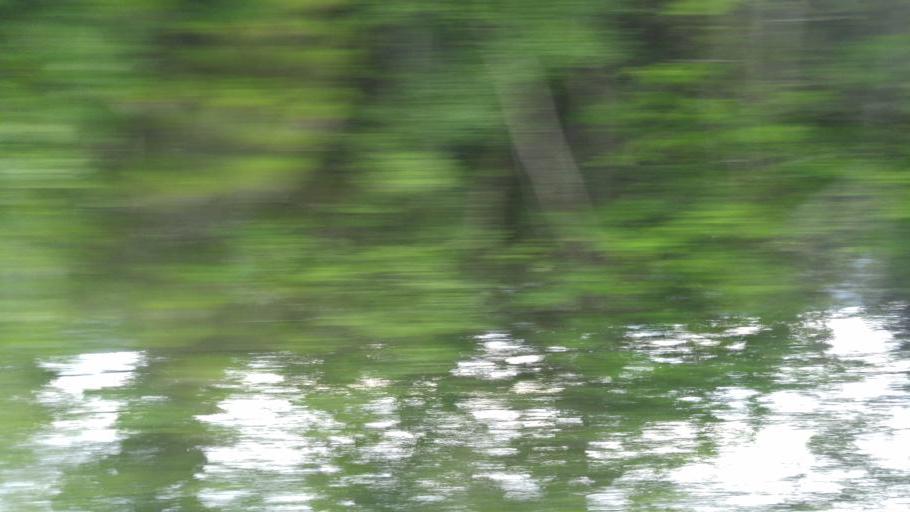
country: NO
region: Nord-Trondelag
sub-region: Meraker
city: Meraker
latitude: 63.4011
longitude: 11.7903
